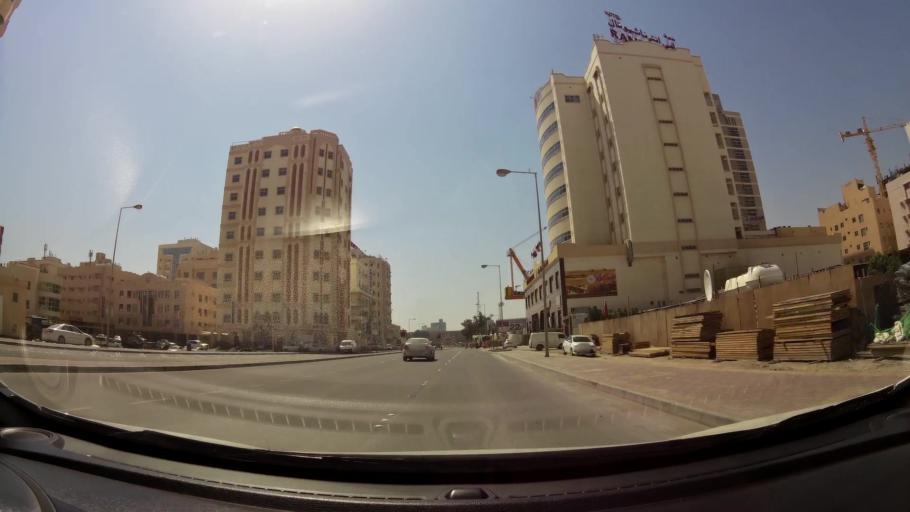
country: BH
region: Manama
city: Manama
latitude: 26.2128
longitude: 50.6098
